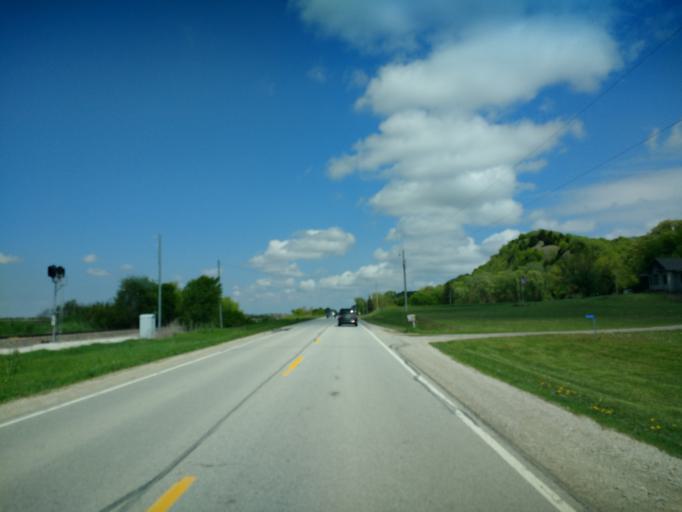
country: US
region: Iowa
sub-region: Harrison County
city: Missouri Valley
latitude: 41.4535
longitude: -95.8739
